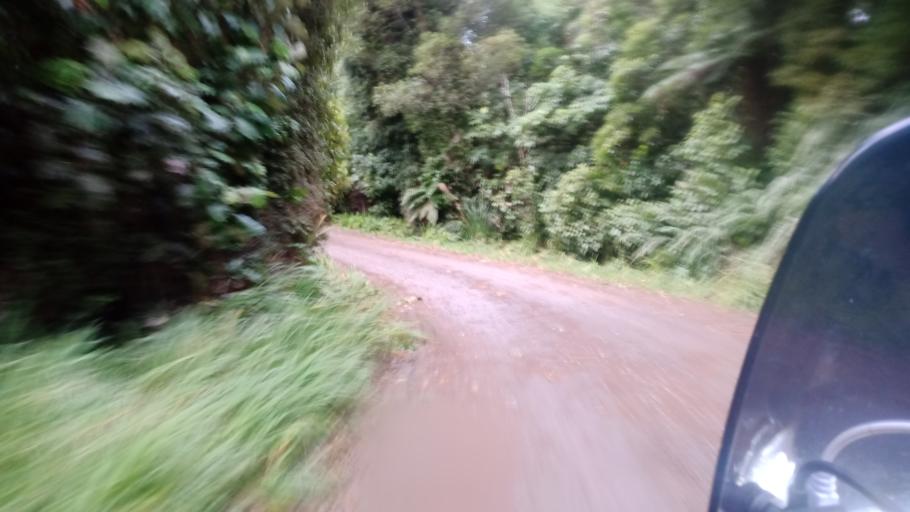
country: NZ
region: Hawke's Bay
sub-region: Wairoa District
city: Wairoa
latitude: -38.7298
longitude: 177.0897
